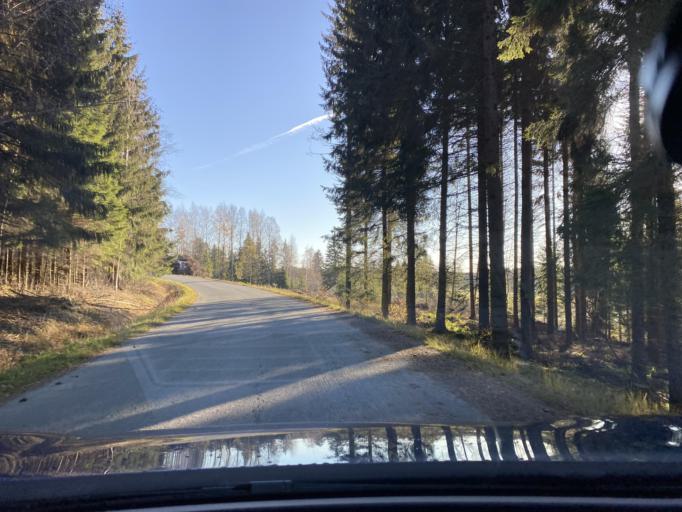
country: FI
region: Pirkanmaa
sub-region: Etelae-Pirkanmaa
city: Akaa
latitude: 61.0099
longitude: 23.8809
